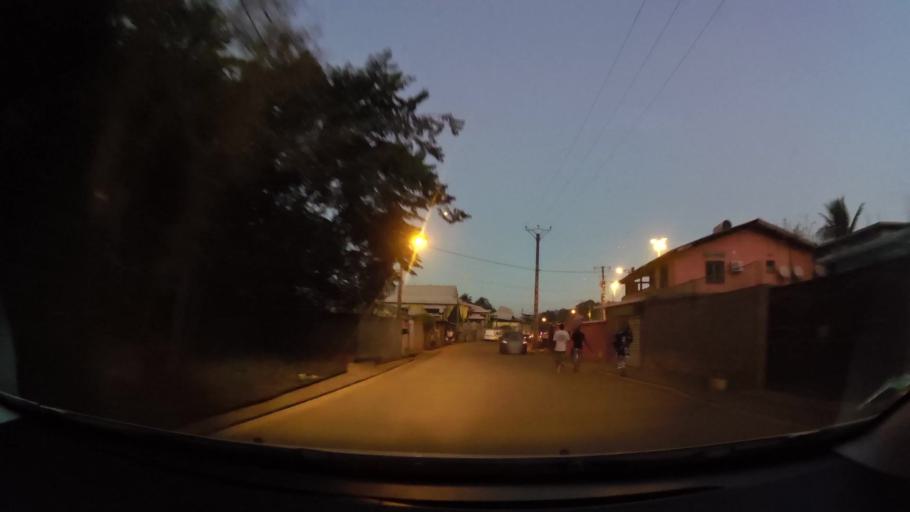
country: YT
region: Bandraboua
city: Bandraboua
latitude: -12.7217
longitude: 45.1172
